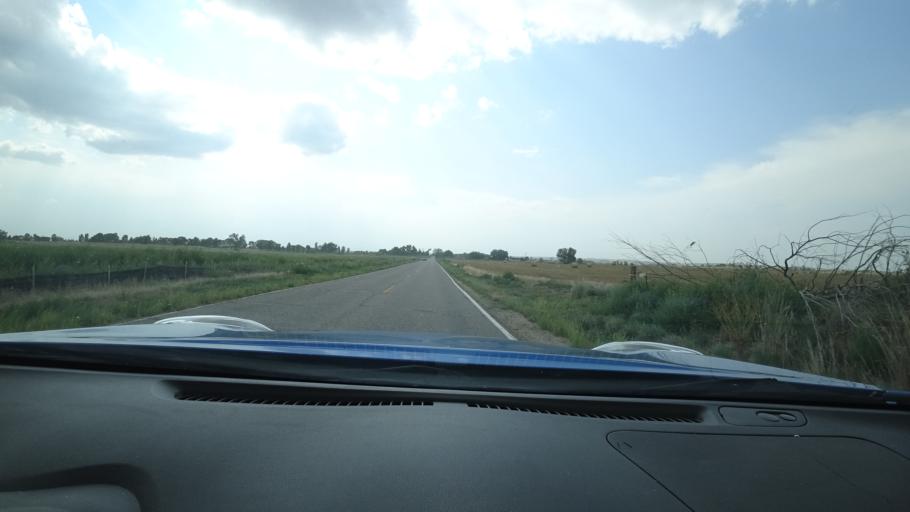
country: US
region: Colorado
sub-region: Adams County
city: Brighton
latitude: 39.9216
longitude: -104.8225
